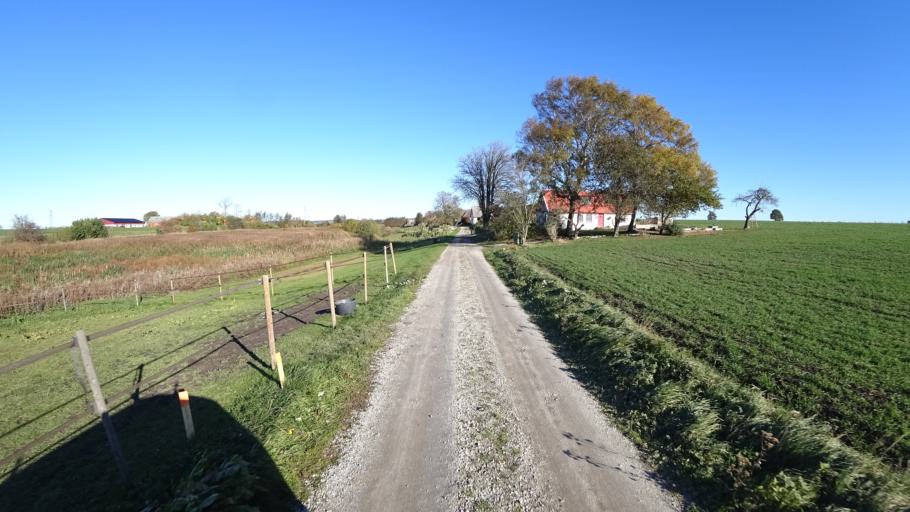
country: SE
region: Skane
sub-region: Lunds Kommun
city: Genarp
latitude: 55.6247
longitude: 13.3321
